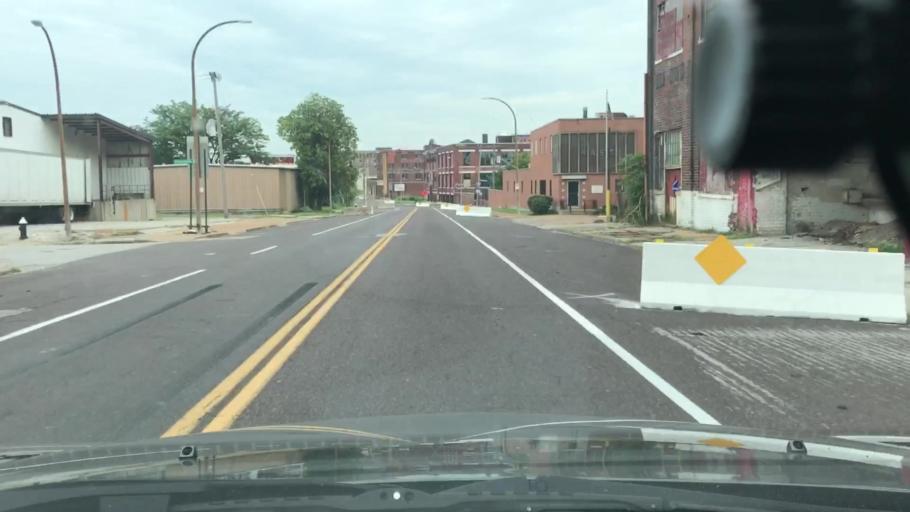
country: US
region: Missouri
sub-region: City of Saint Louis
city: St. Louis
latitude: 38.6443
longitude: -90.1866
